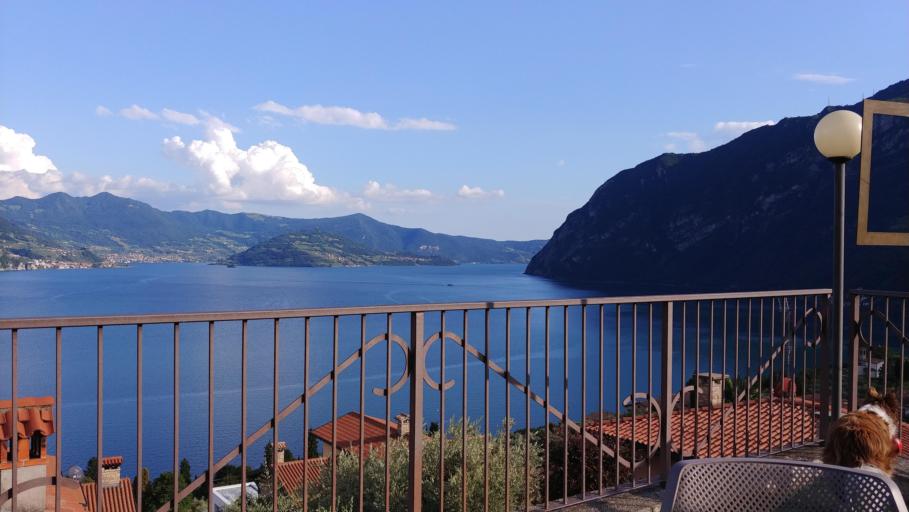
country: IT
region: Lombardy
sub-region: Provincia di Bergamo
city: Riva di Solto
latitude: 45.7809
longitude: 10.0445
